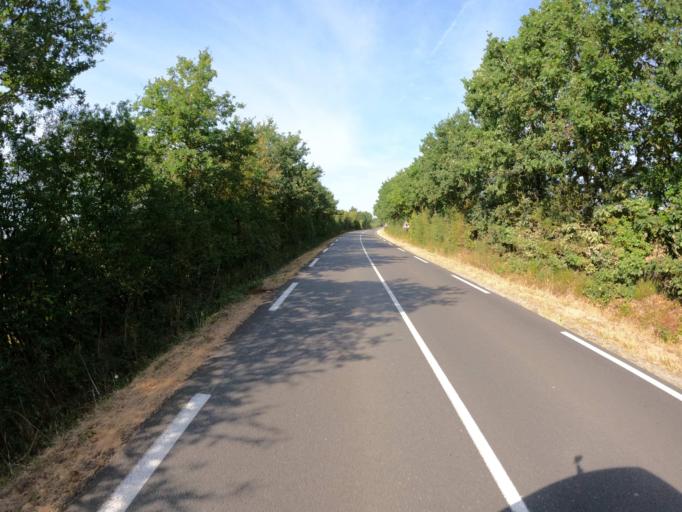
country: FR
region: Pays de la Loire
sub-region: Departement de la Vendee
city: Froidfond
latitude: 46.8487
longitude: -1.7323
